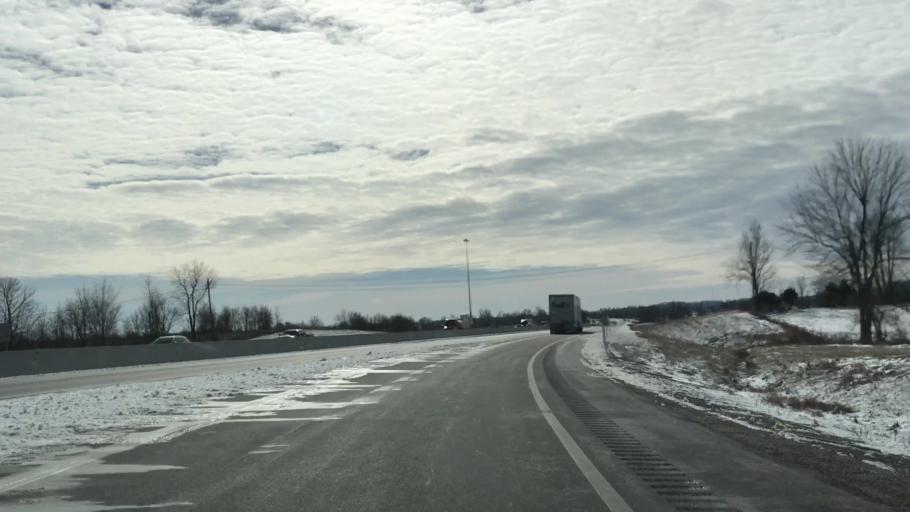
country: US
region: Kentucky
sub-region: Larue County
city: Hodgenville
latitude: 37.5191
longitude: -85.8857
